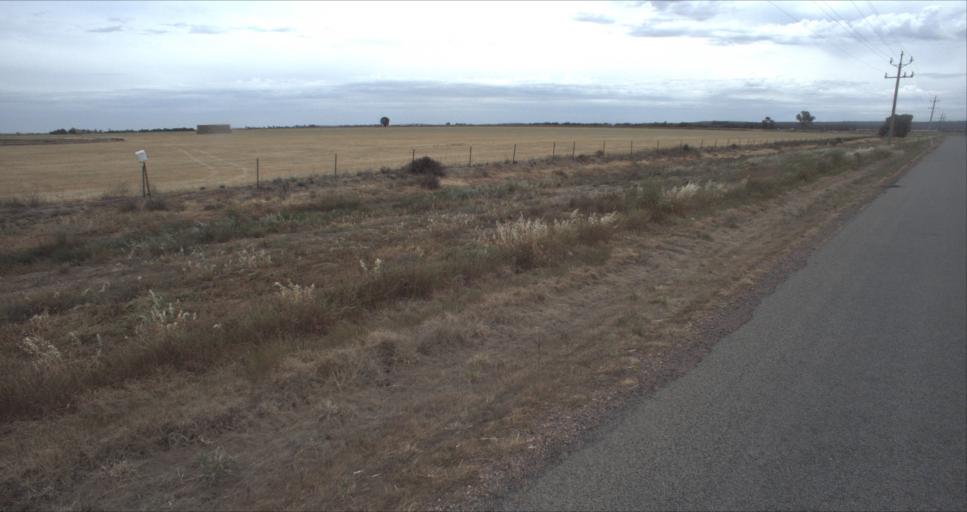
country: AU
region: New South Wales
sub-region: Leeton
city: Leeton
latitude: -34.4889
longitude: 146.4019
